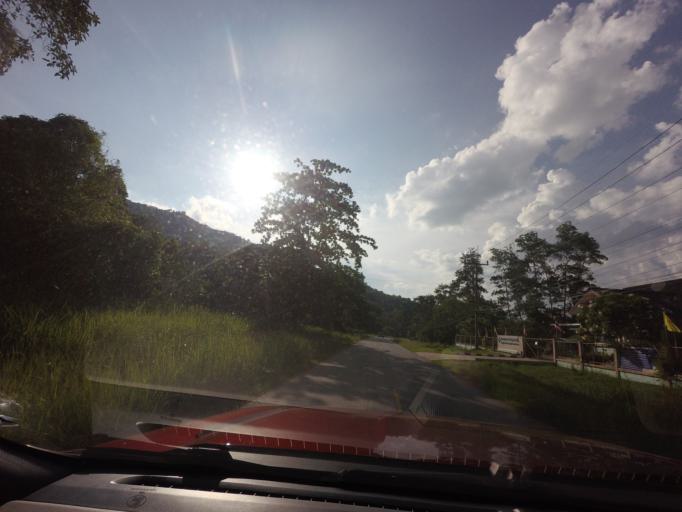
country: TH
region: Yala
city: Than To
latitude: 6.2044
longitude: 101.2363
